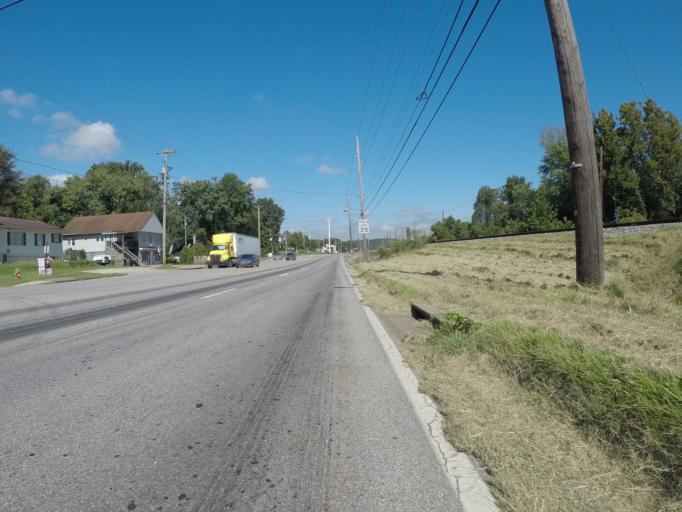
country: US
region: Ohio
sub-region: Lawrence County
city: South Point
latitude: 38.4354
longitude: -82.6069
